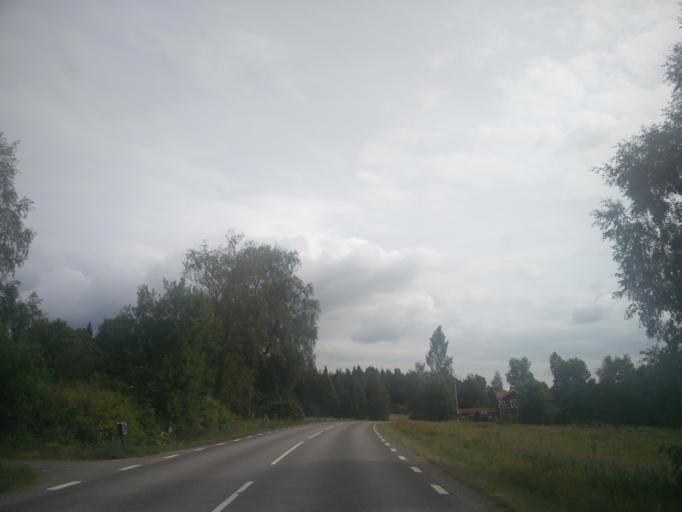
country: SE
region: Vaermland
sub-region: Arvika Kommun
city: Arvika
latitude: 59.7379
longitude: 12.5597
